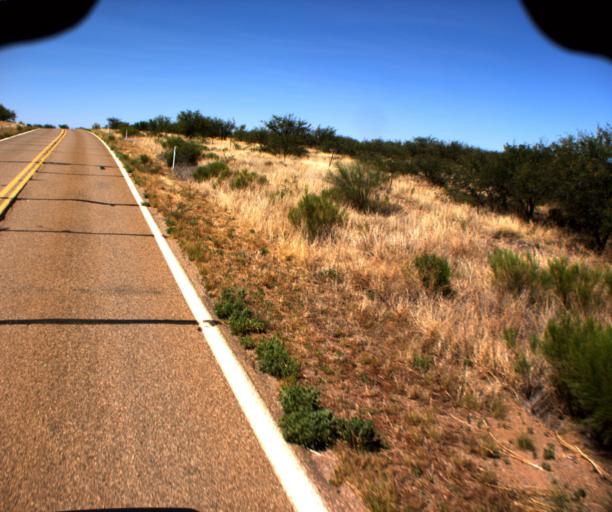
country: US
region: Arizona
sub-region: Pima County
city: Three Points
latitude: 31.6907
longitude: -111.4872
